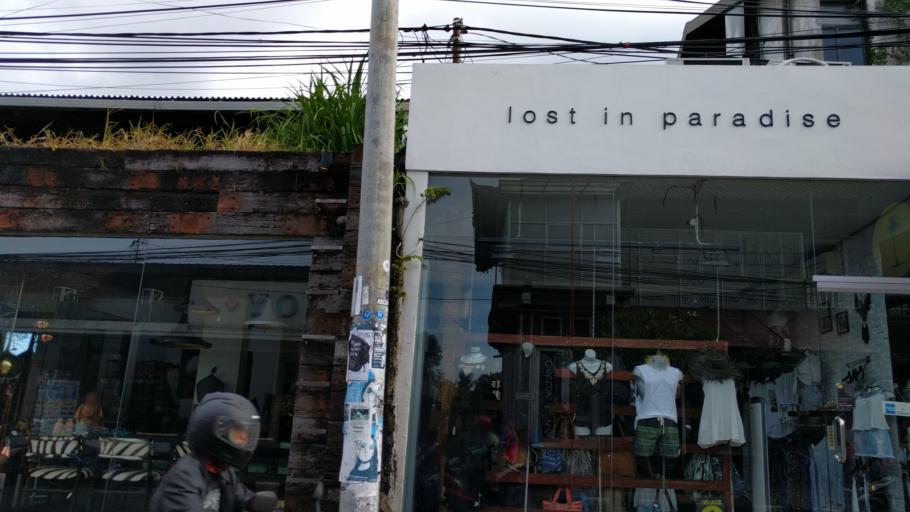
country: ID
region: Bali
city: Kuta
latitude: -8.6835
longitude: 115.1642
